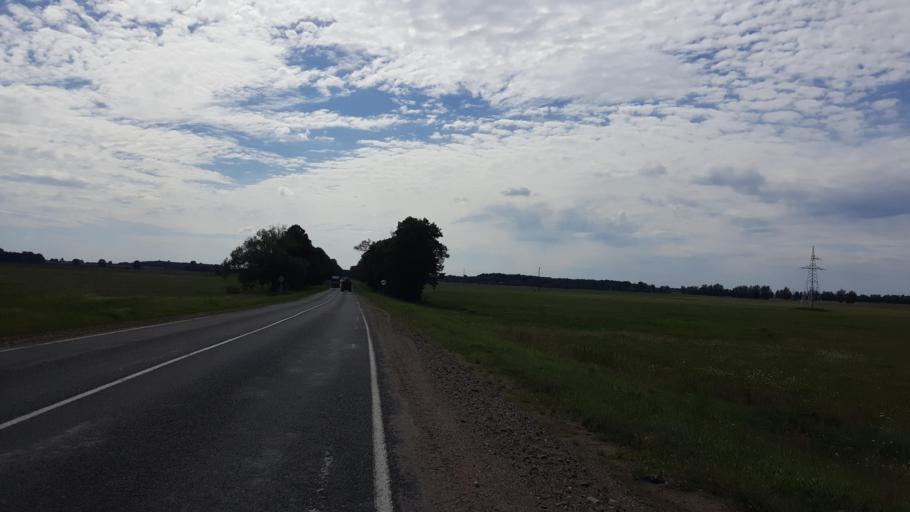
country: BY
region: Brest
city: Zhabinka
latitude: 52.3093
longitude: 23.9229
